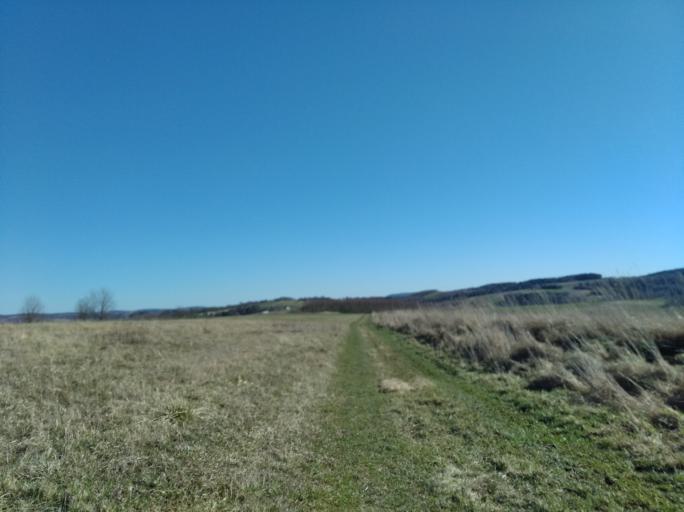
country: PL
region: Subcarpathian Voivodeship
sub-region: Powiat strzyzowski
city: Wisniowa
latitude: 49.9157
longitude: 21.6816
